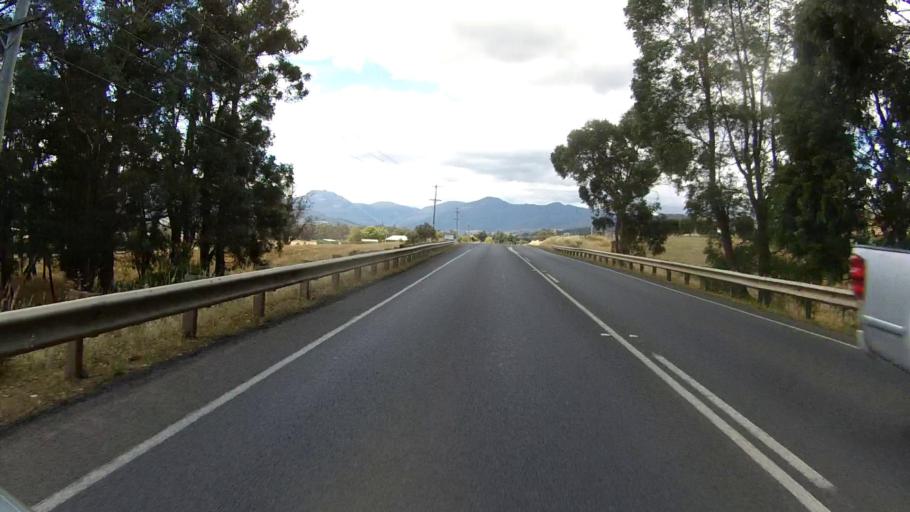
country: AU
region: Tasmania
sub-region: Huon Valley
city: Huonville
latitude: -42.9922
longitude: 147.0789
